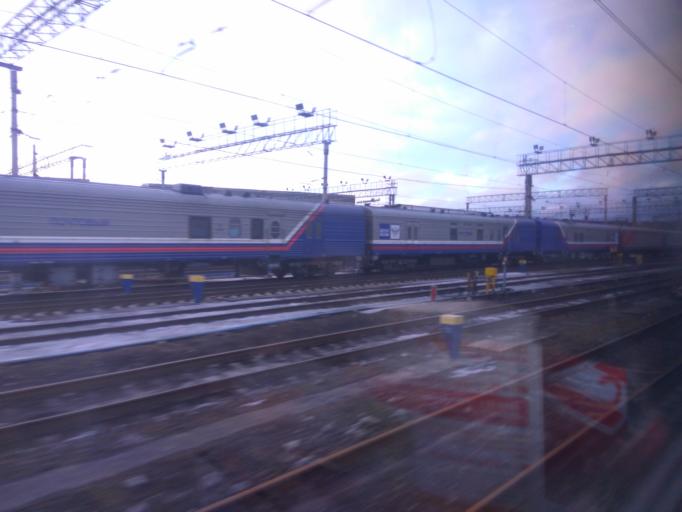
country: RU
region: St.-Petersburg
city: Centralniy
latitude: 59.9191
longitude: 30.3665
